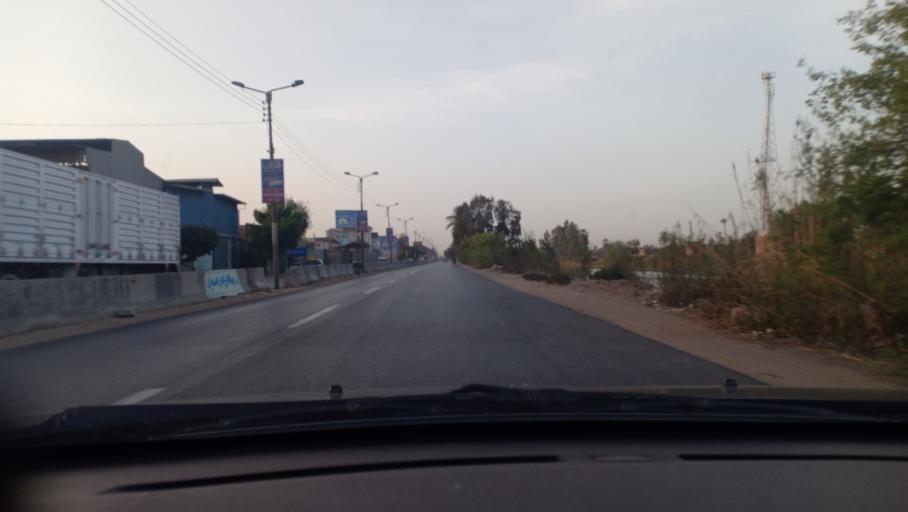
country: EG
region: Muhafazat al Gharbiyah
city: Zifta
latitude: 30.6476
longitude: 31.2827
